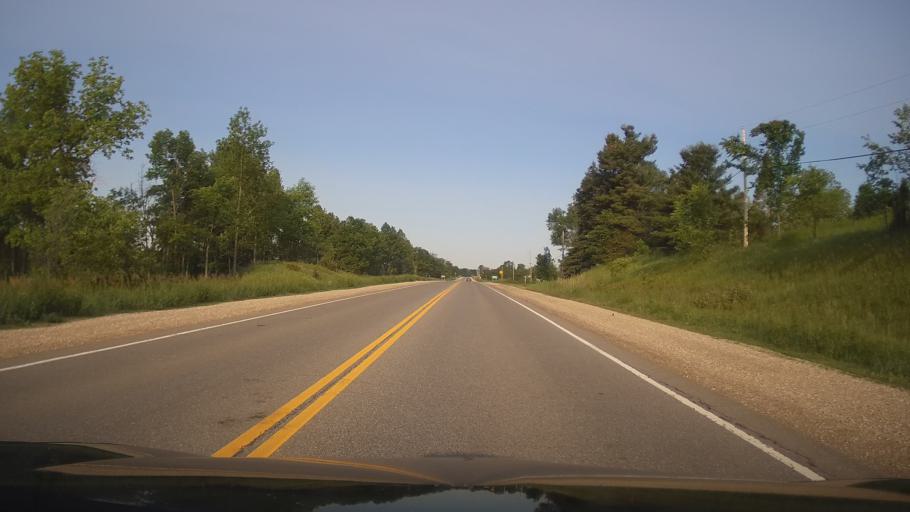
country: CA
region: Ontario
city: Perth
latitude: 44.8720
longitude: -76.3714
